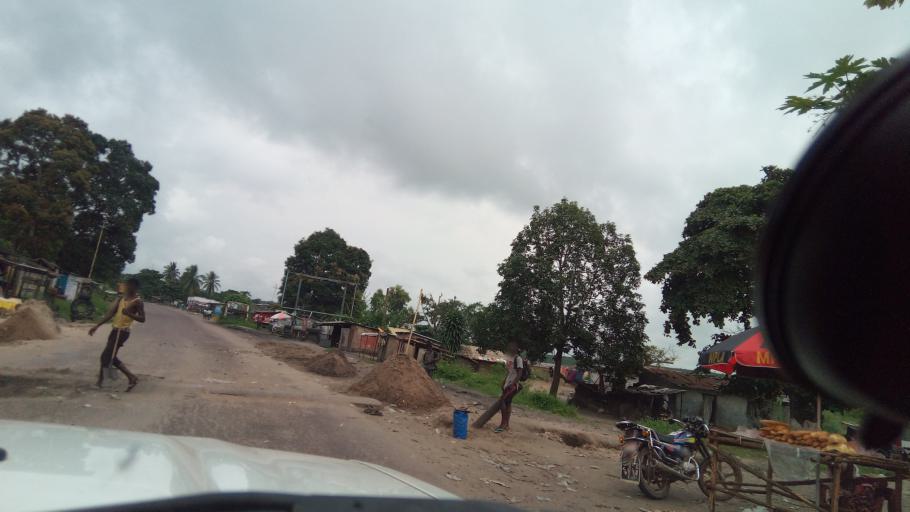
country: CD
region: Bas-Congo
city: Kasangulu
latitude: -4.8277
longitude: 15.1811
